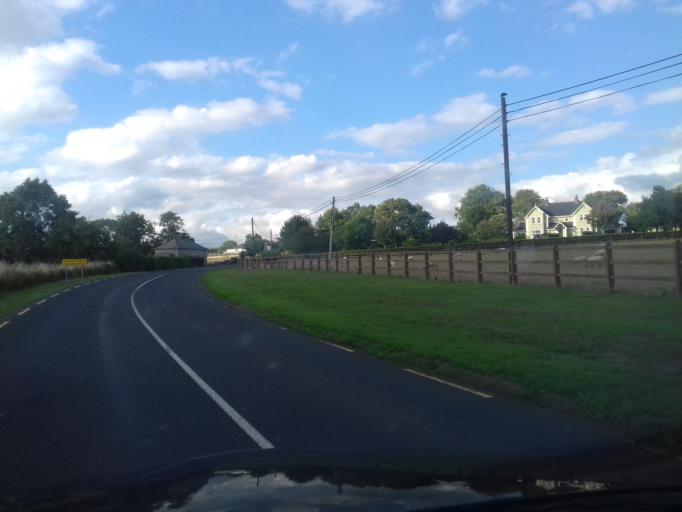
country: IE
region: Leinster
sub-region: Loch Garman
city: New Ross
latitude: 52.4496
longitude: -6.9629
